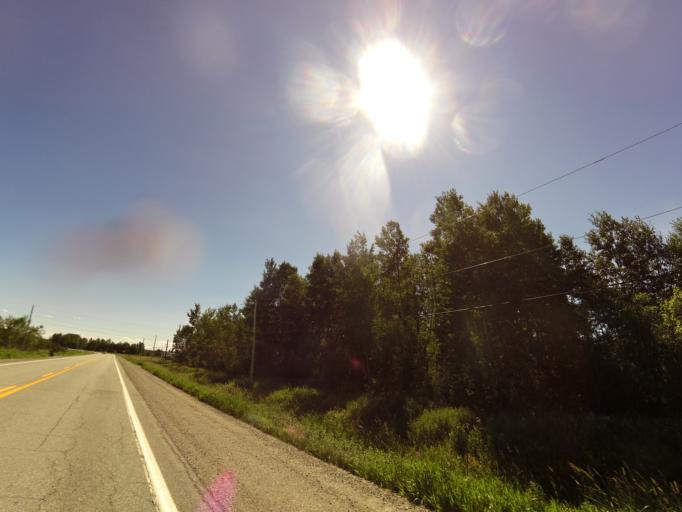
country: CA
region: Quebec
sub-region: Abitibi-Temiscamingue
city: Senneterre
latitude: 48.2541
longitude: -77.3351
